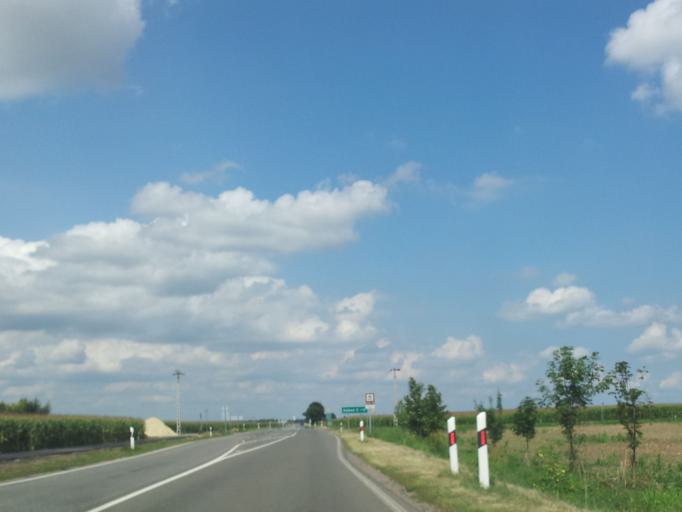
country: HU
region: Baranya
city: Mohacs
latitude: 45.9506
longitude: 18.6668
